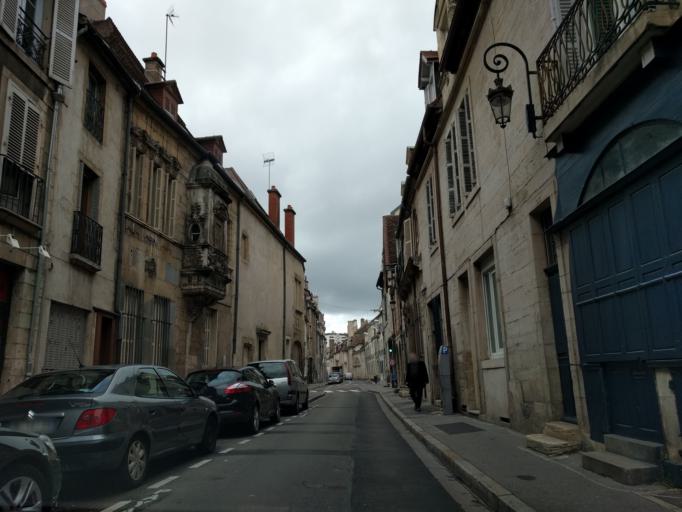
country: FR
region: Bourgogne
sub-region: Departement de la Cote-d'Or
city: Dijon
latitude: 47.3223
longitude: 5.0454
